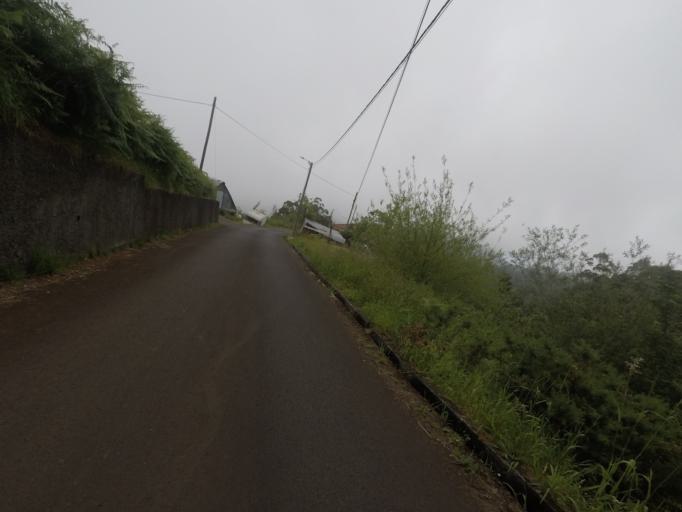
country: PT
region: Madeira
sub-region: Santana
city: Santana
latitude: 32.7465
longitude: -16.8798
